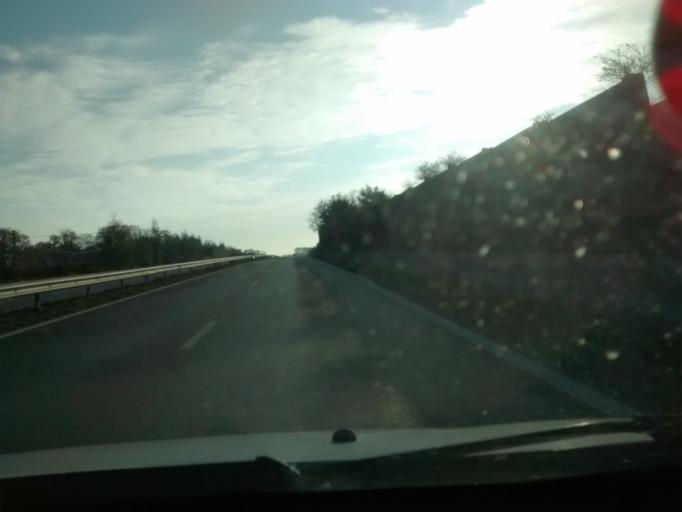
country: FR
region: Brittany
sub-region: Departement d'Ille-et-Vilaine
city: Chevaigne
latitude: 48.1942
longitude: -1.6223
